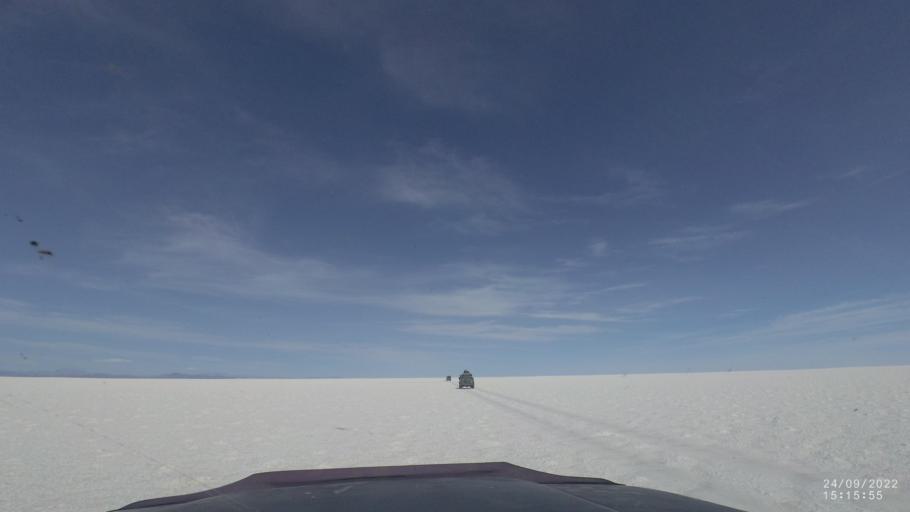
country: BO
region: Potosi
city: Colchani
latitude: -19.9776
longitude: -67.4404
